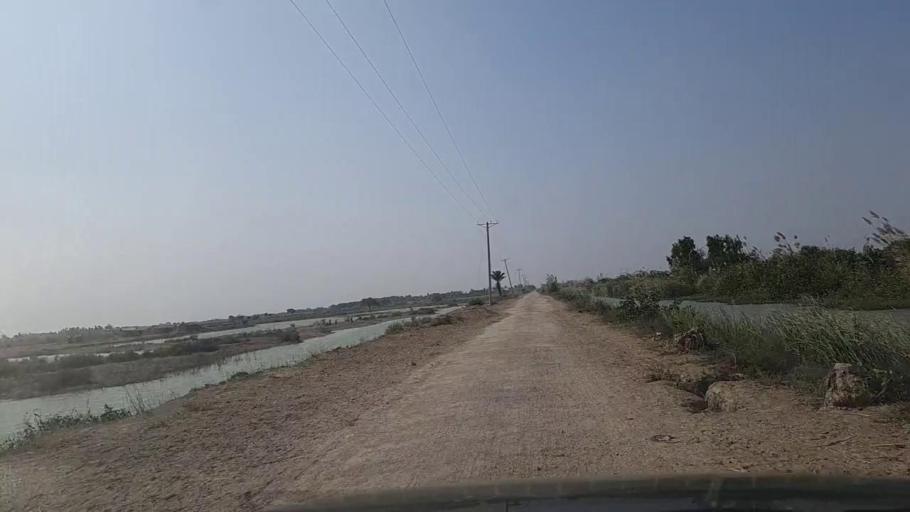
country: PK
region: Sindh
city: Gharo
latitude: 24.6840
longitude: 67.6011
